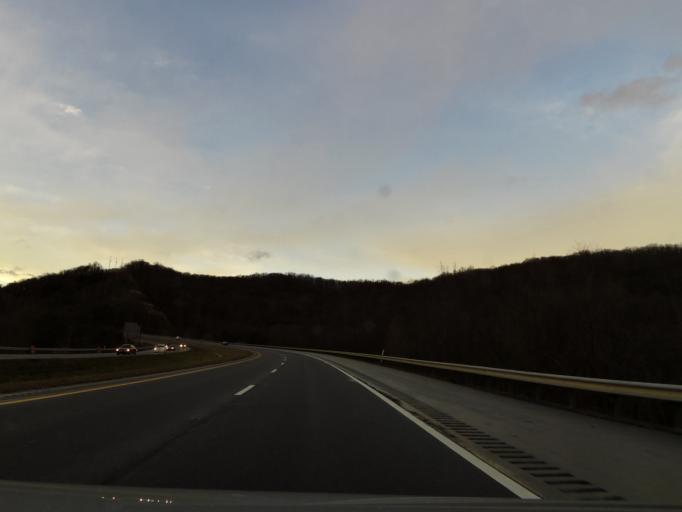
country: US
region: Tennessee
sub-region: Campbell County
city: Jacksboro
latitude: 36.3899
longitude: -84.2547
